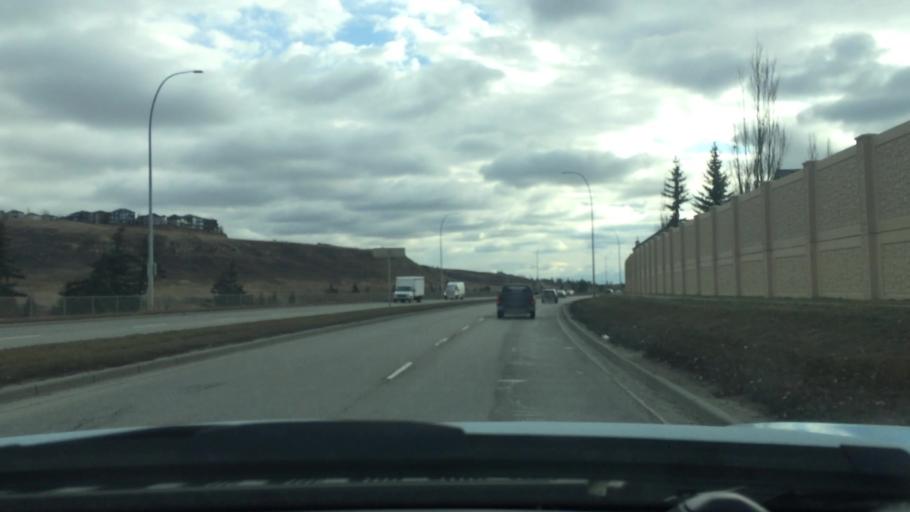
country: CA
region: Alberta
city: Calgary
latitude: 51.1527
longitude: -114.1032
